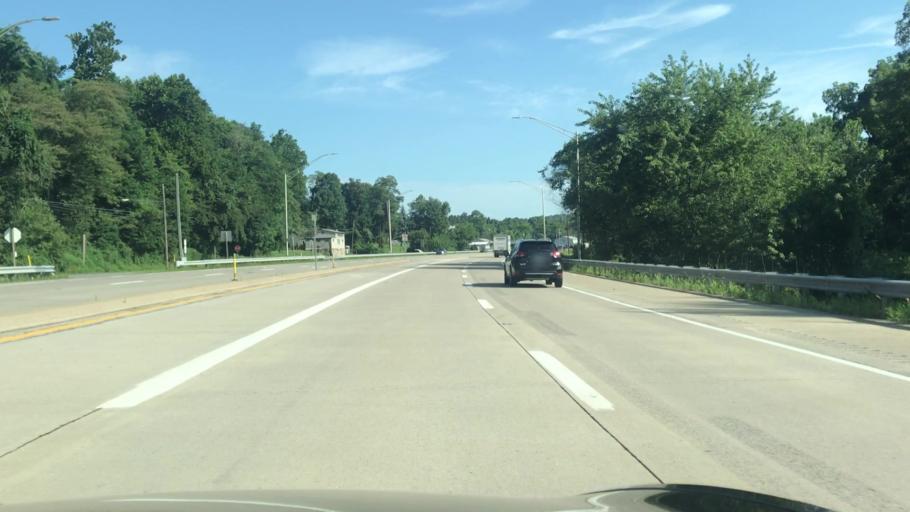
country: US
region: Pennsylvania
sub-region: Dauphin County
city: Millersburg
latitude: 40.5622
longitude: -76.9934
